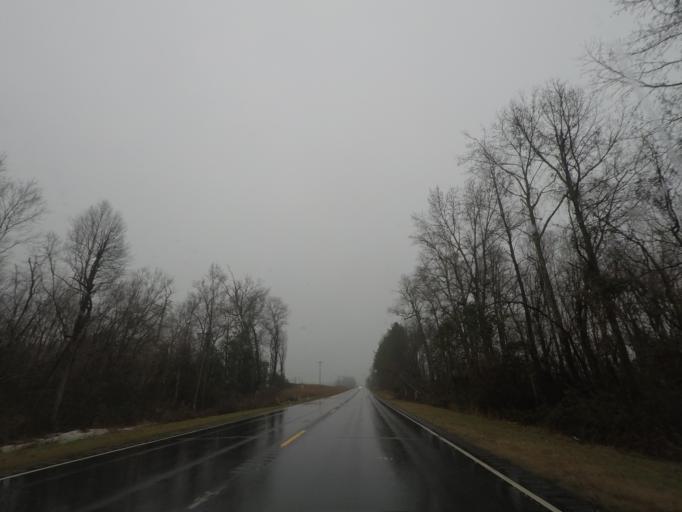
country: US
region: North Carolina
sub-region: Scotland County
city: Laurinburg
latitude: 34.8340
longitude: -79.4593
